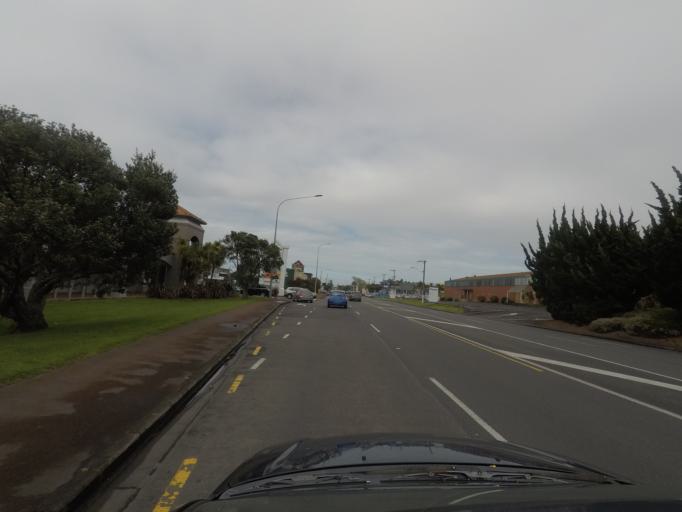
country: NZ
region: Auckland
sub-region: Auckland
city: Tamaki
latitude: -36.8985
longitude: 174.8449
